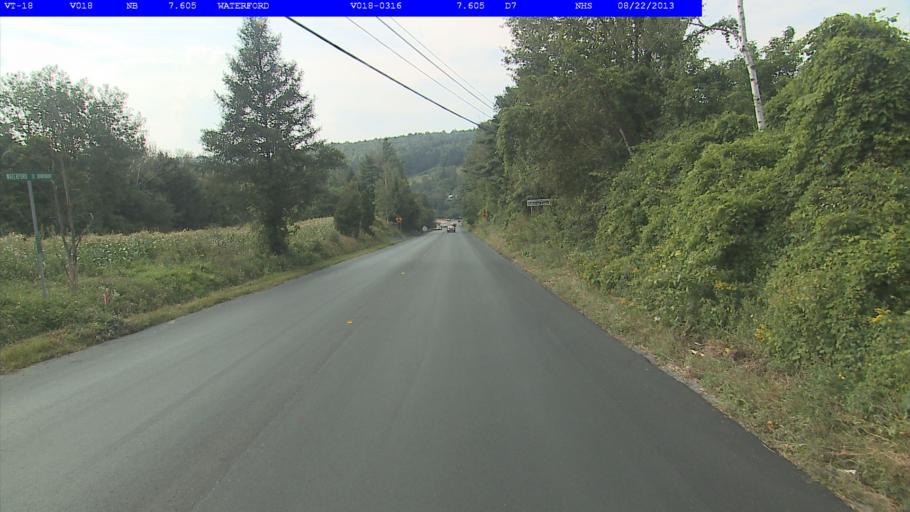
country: US
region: Vermont
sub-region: Caledonia County
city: St Johnsbury
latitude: 44.4273
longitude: -71.9591
